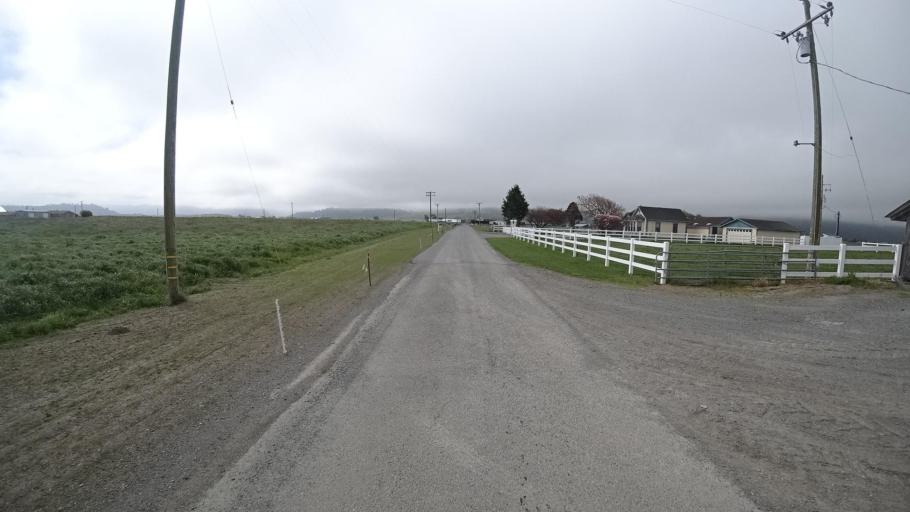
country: US
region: California
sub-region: Humboldt County
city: Fortuna
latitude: 40.5790
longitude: -124.1878
